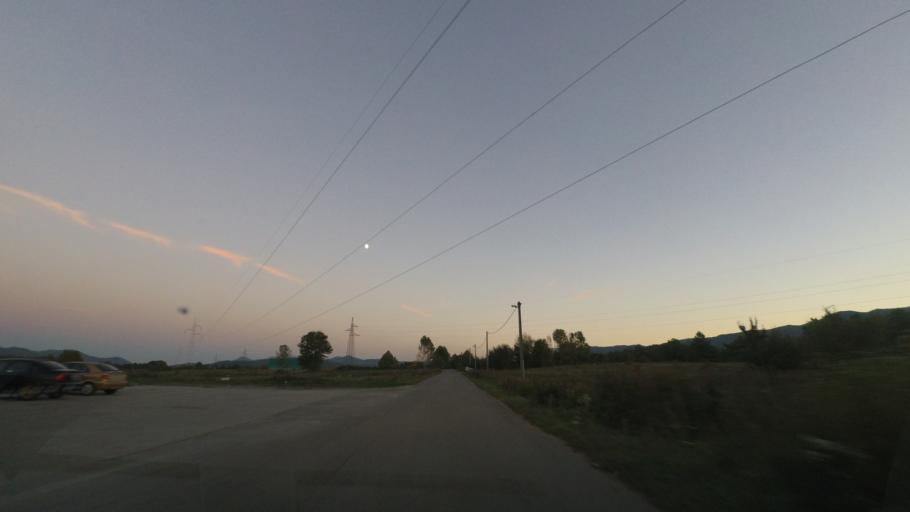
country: HR
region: Zadarska
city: Obrovac
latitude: 44.3700
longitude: 15.6473
